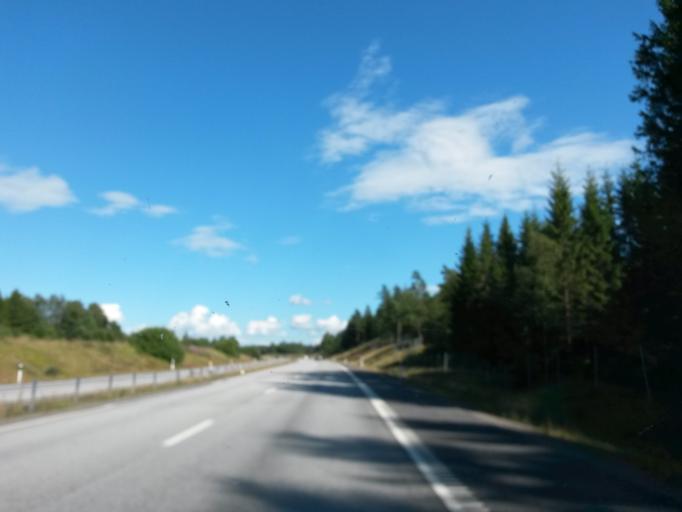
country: SE
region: Vaestra Goetaland
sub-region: Trollhattan
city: Sjuntorp
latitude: 58.3277
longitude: 12.1422
